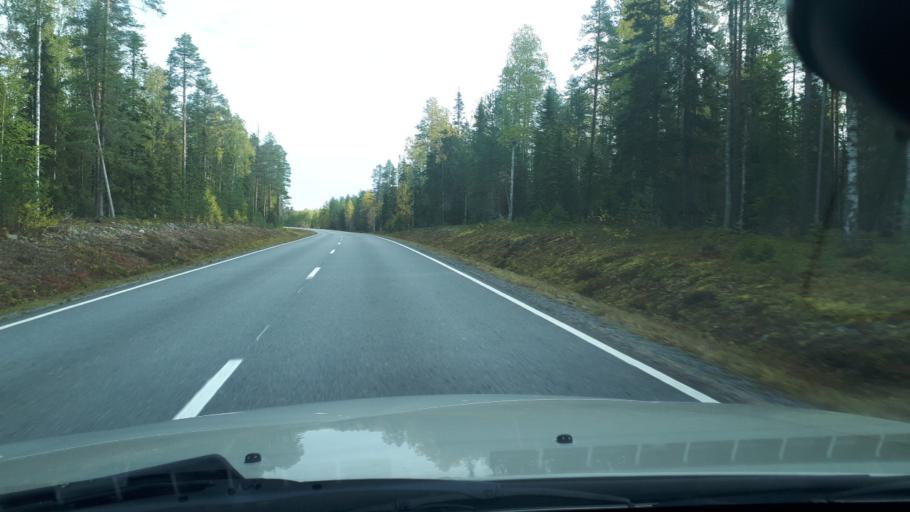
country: FI
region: Northern Ostrobothnia
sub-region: Oulu
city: Yli-Ii
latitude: 65.9287
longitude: 25.8568
